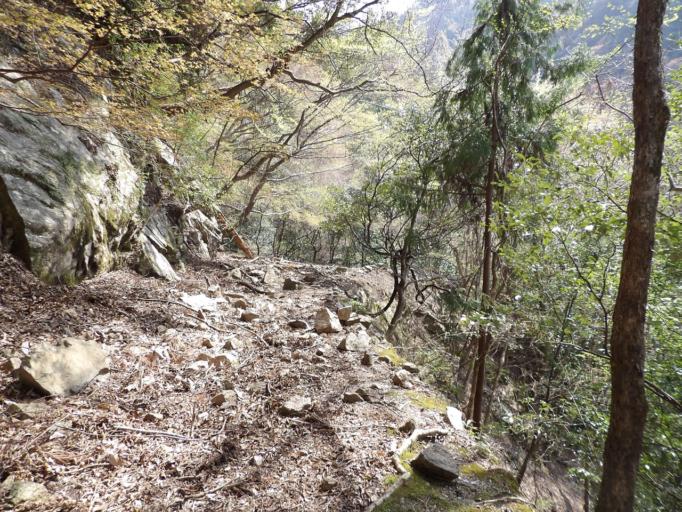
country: JP
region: Shizuoka
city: Mori
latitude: 35.1475
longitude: 137.8239
